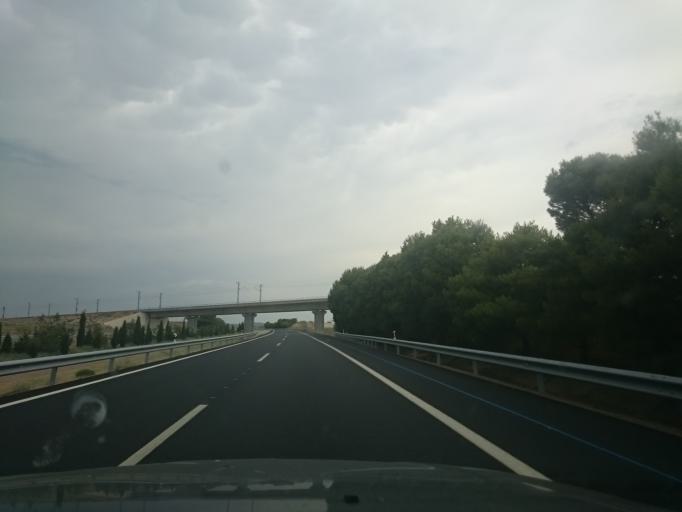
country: ES
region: Aragon
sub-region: Provincia de Zaragoza
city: Pina de Ebro
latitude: 41.5315
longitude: -0.5096
